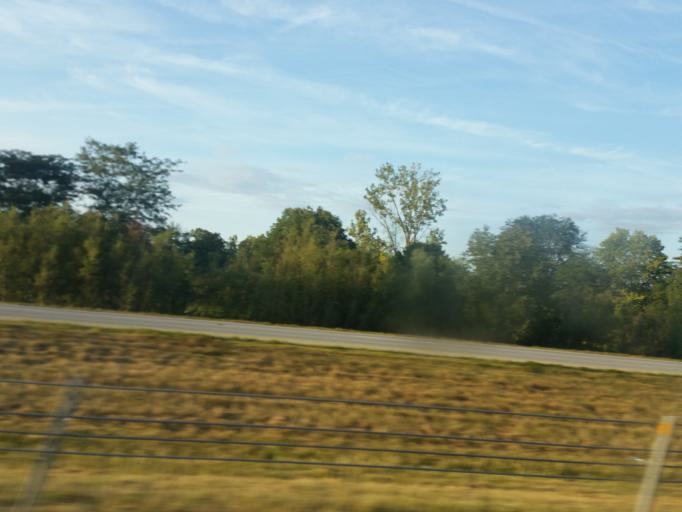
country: US
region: Indiana
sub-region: Boone County
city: Zionsville
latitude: 39.9313
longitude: -86.3057
